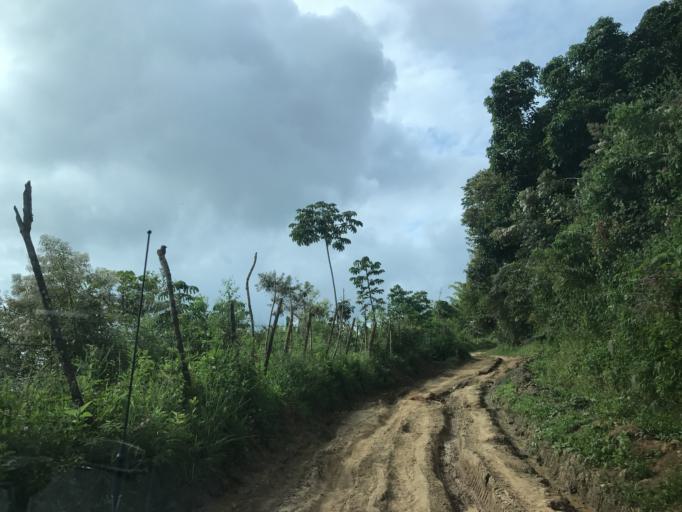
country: CO
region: Valle del Cauca
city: Obando
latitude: 4.5692
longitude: -75.8920
